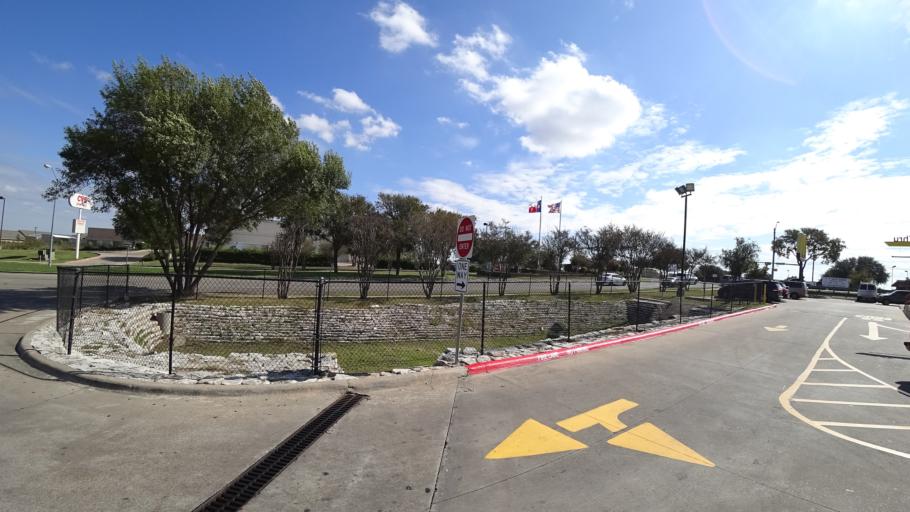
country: US
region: Texas
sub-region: Travis County
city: Windemere
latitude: 30.4481
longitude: -97.6395
